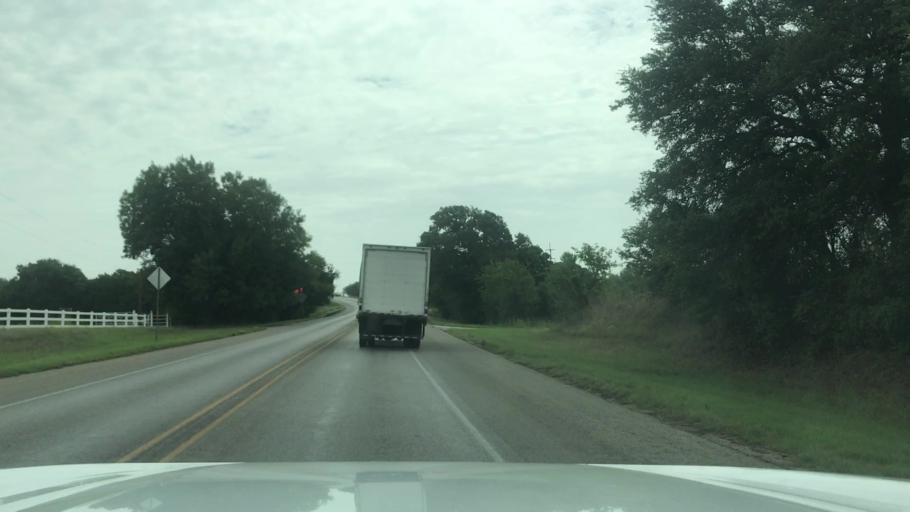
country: US
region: Texas
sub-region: Comanche County
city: De Leon
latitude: 32.1022
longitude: -98.4790
